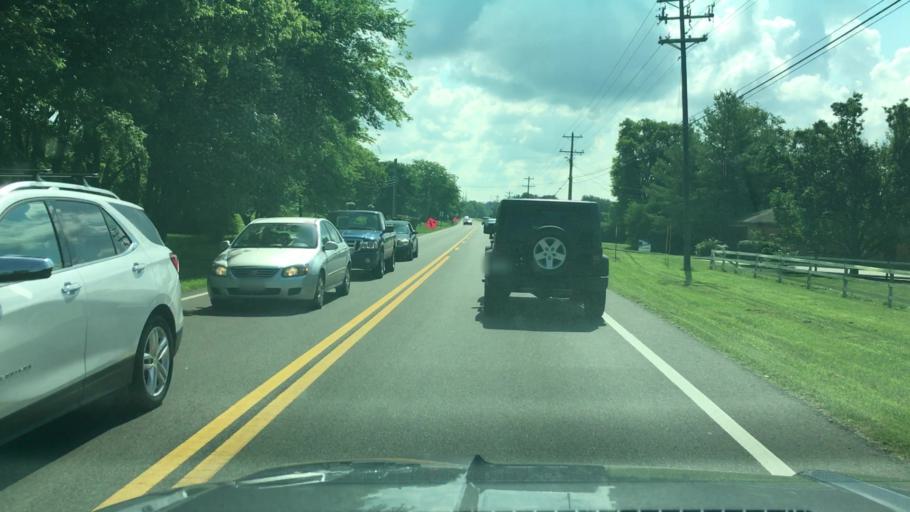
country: US
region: Tennessee
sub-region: Williamson County
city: Nolensville
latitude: 35.8679
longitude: -86.7094
